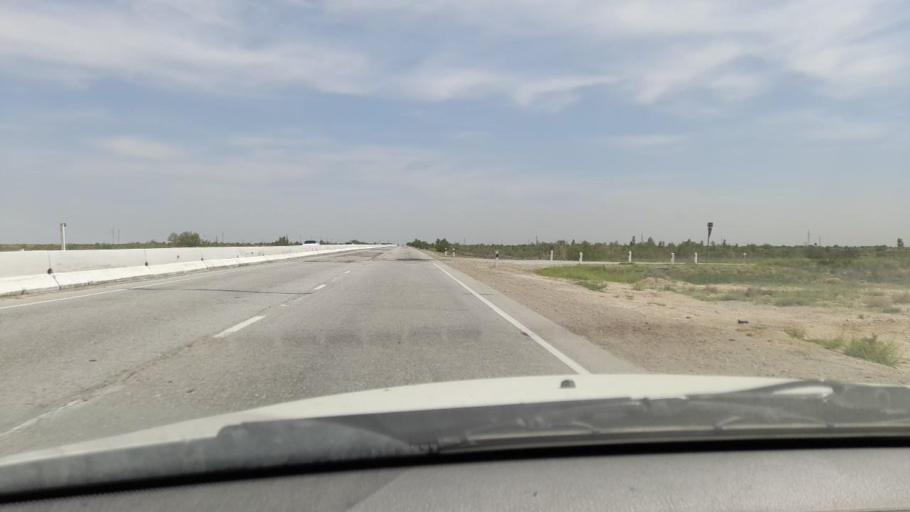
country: UZ
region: Navoiy
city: Qiziltepa
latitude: 40.0851
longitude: 64.9493
